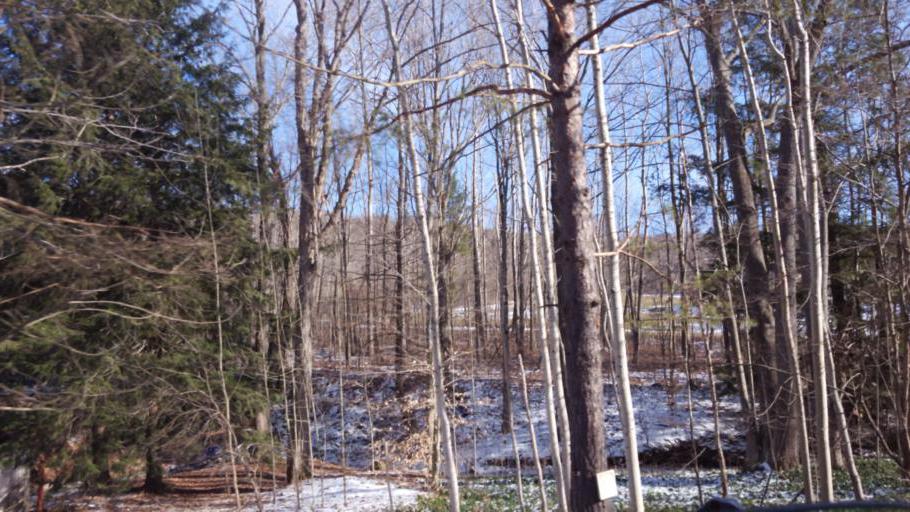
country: US
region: New York
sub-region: Allegany County
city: Wellsville
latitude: 42.0912
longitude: -77.9876
